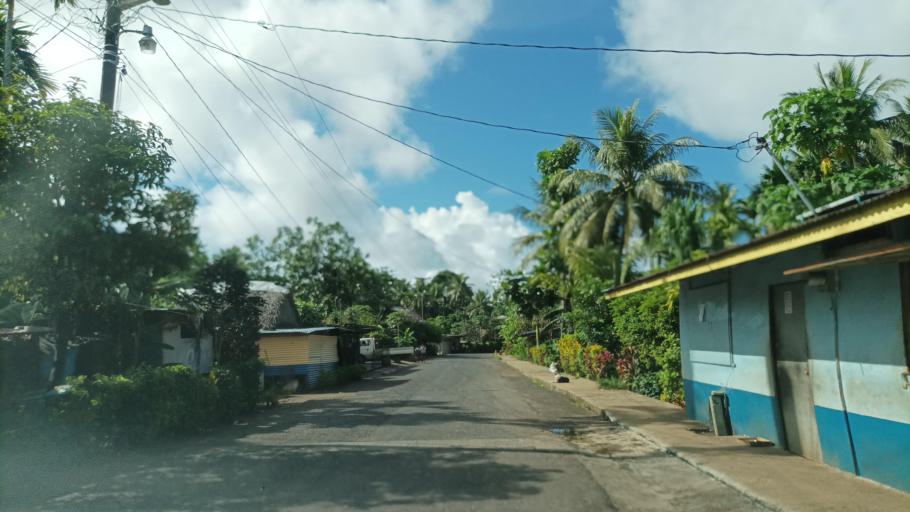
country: FM
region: Pohnpei
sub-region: Kolonia Municipality
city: Kolonia Town
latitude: 6.9626
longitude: 158.2050
